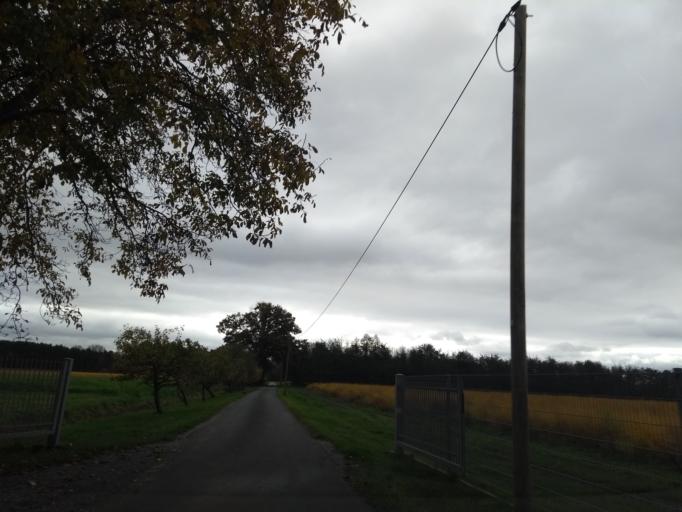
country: DE
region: North Rhine-Westphalia
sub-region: Regierungsbezirk Detmold
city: Hovelhof
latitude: 51.7659
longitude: 8.6764
